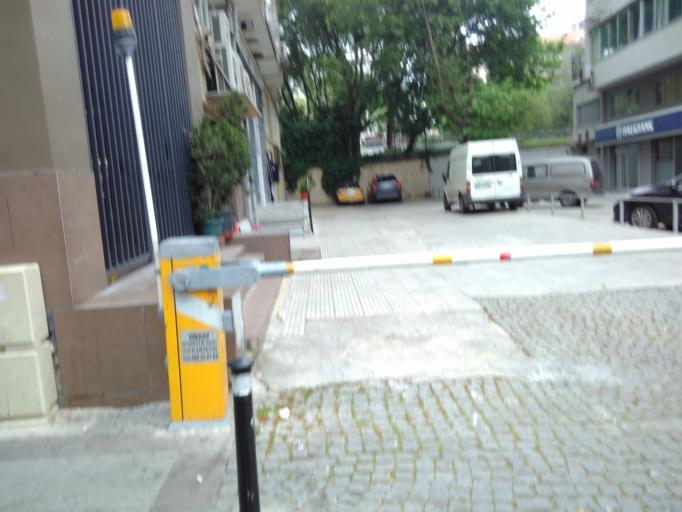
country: TR
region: Istanbul
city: Sisli
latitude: 41.0419
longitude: 28.9868
